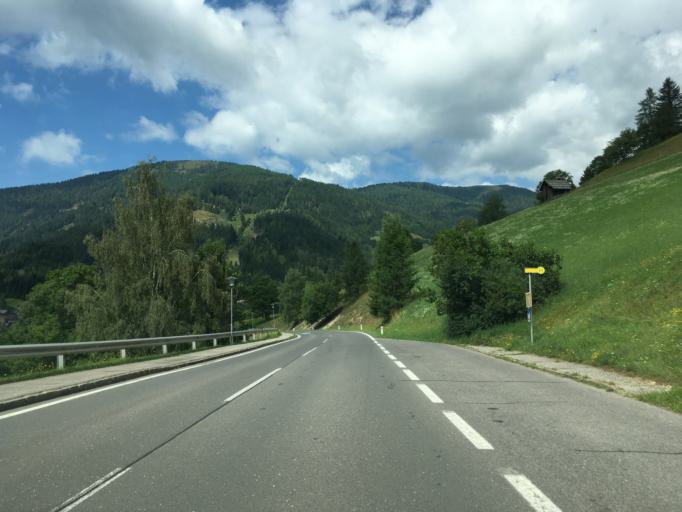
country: AT
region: Carinthia
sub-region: Politischer Bezirk Spittal an der Drau
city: Kleinkirchheim
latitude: 46.8169
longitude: 13.7810
